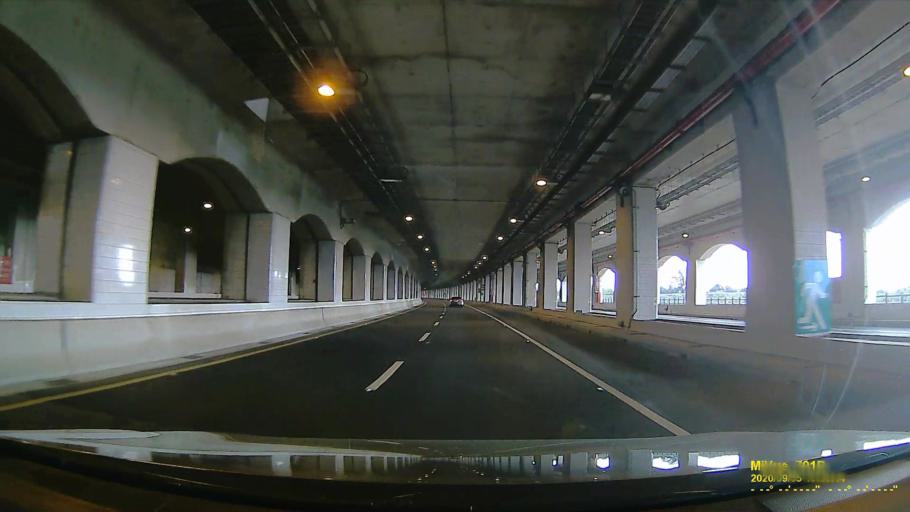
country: TW
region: Taiwan
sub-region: Hsinchu
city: Zhubei
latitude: 24.8936
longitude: 120.9621
